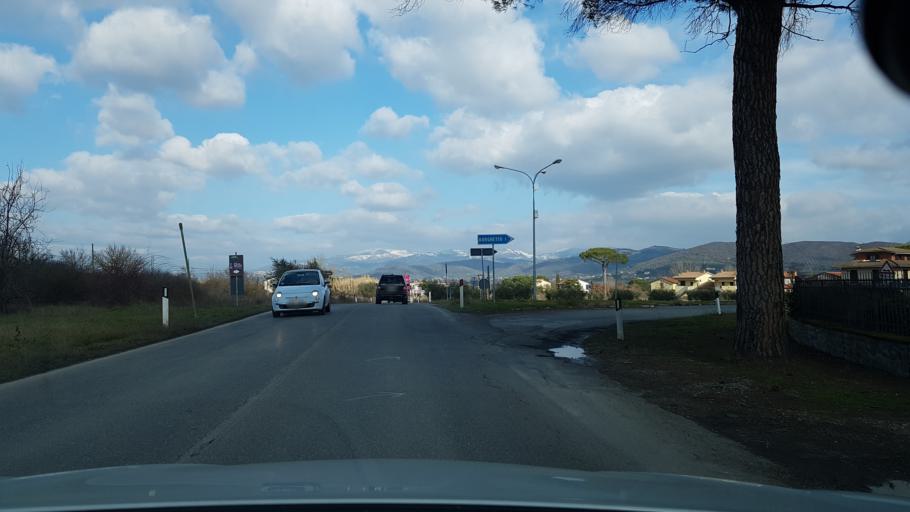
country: IT
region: Tuscany
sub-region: Province of Arezzo
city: Terontola
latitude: 43.1805
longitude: 12.0136
